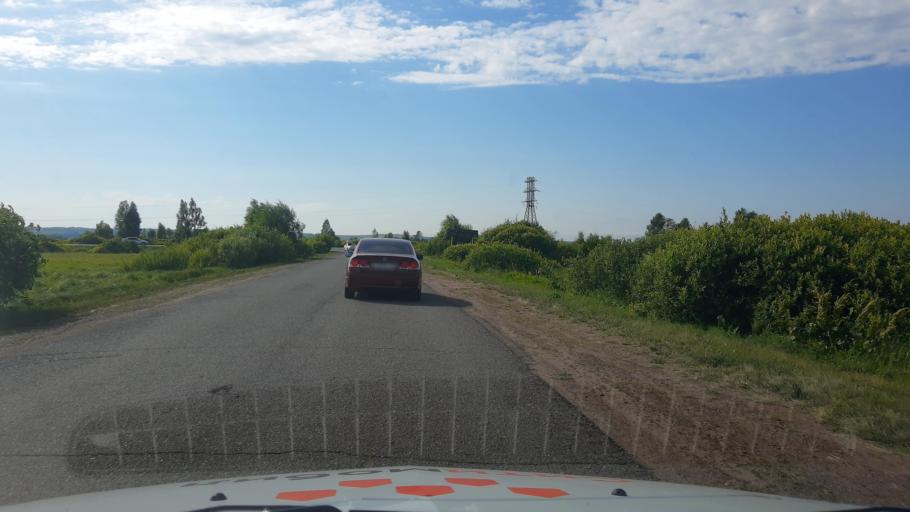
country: RU
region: Bashkortostan
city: Mikhaylovka
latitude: 54.9785
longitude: 55.7722
